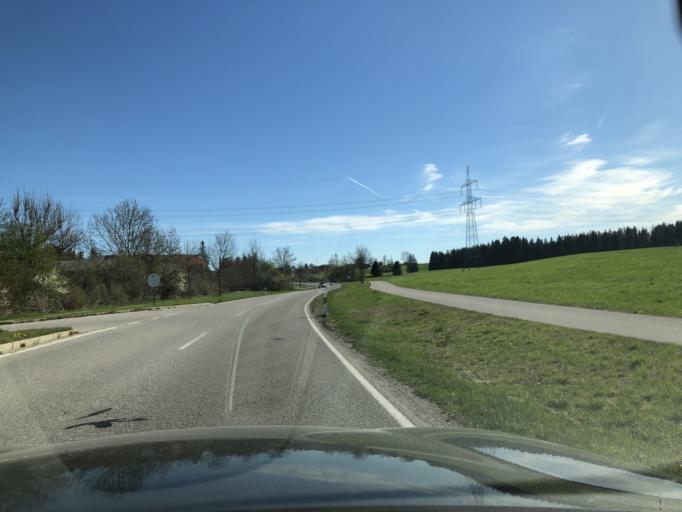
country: DE
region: Bavaria
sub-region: Swabia
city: Nesselwang
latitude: 47.6305
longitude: 10.5159
